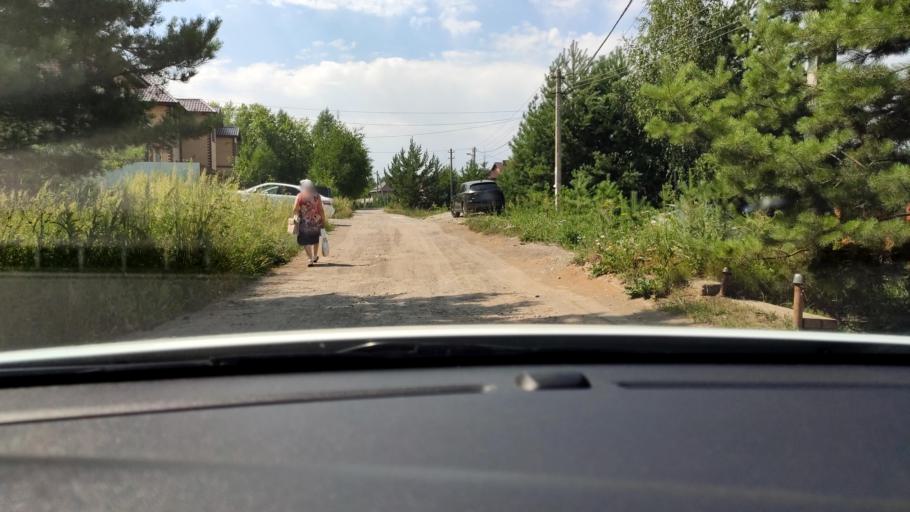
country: RU
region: Tatarstan
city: Stolbishchi
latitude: 55.7440
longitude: 49.2533
